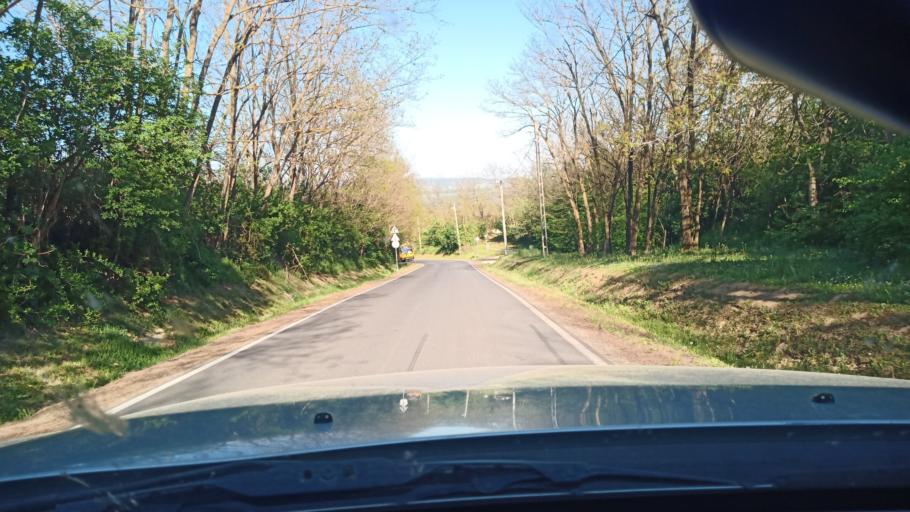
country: HU
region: Zala
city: Heviz
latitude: 46.7640
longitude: 17.1638
